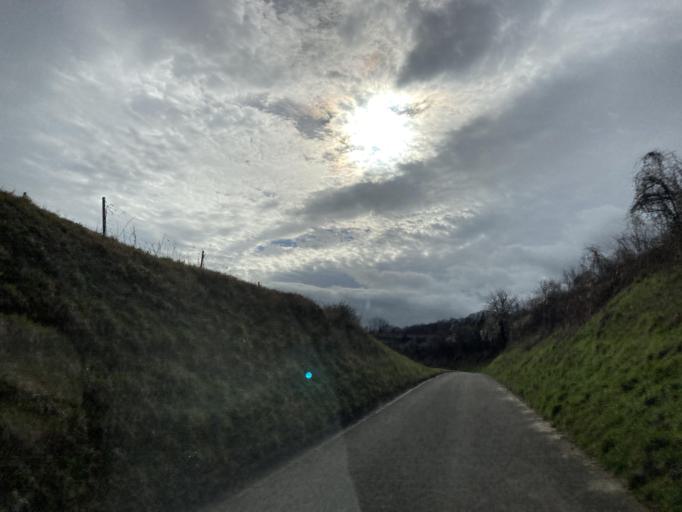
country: DE
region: Baden-Wuerttemberg
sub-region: Freiburg Region
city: Endingen
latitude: 48.1281
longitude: 7.7060
